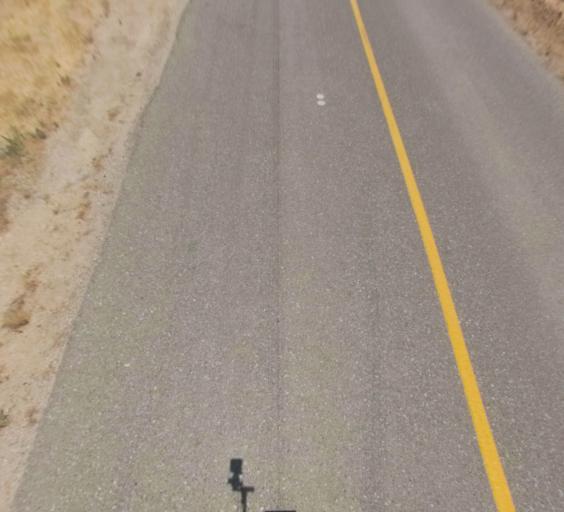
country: US
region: California
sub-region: Madera County
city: Madera Acres
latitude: 37.0617
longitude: -120.0158
